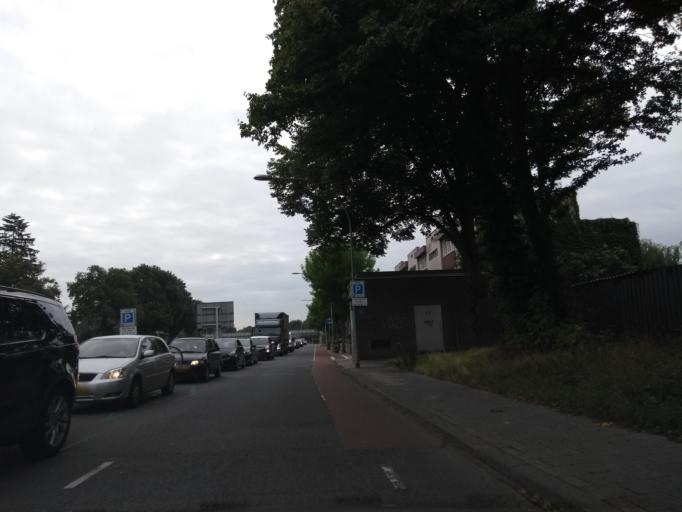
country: NL
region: Overijssel
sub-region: Gemeente Almelo
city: Almelo
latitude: 52.3619
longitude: 6.6686
